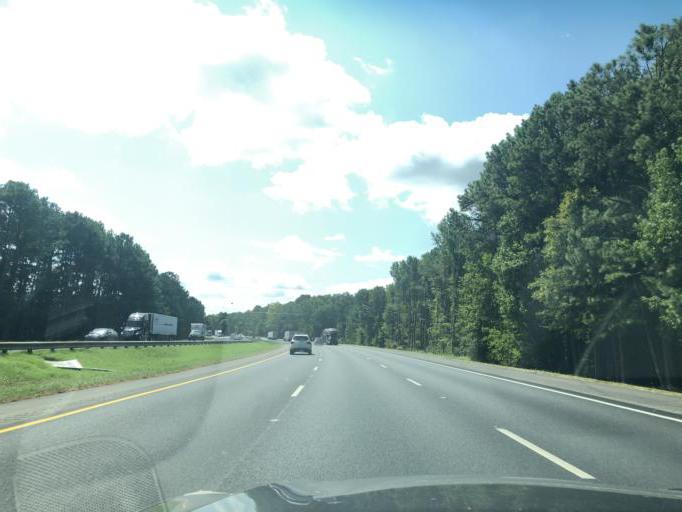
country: US
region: Georgia
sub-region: Whitfield County
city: Dalton
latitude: 34.6724
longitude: -84.9976
